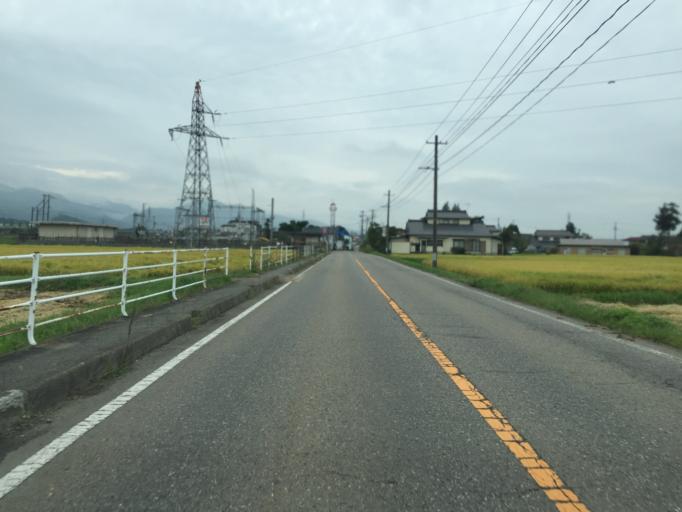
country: JP
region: Fukushima
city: Kitakata
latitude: 37.5324
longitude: 139.9314
